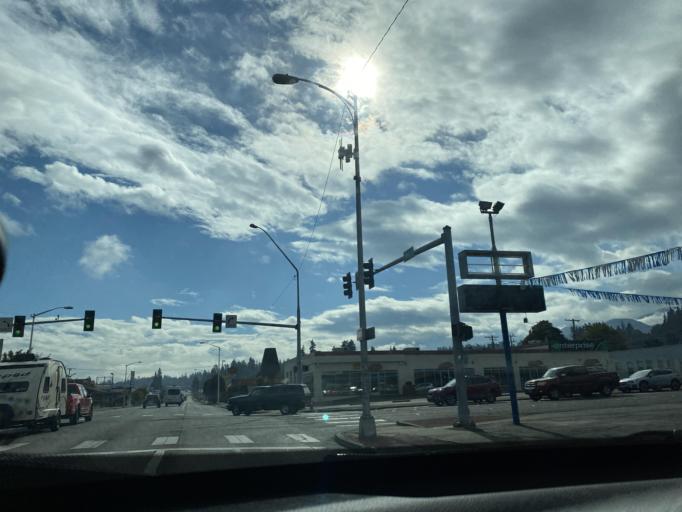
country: US
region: Washington
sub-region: Clallam County
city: Port Angeles
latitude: 48.1132
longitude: -123.4193
